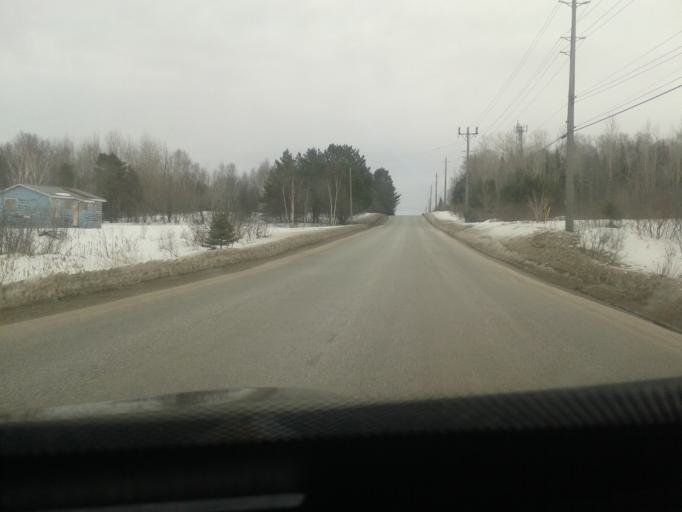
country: CA
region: Ontario
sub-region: Nipissing District
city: North Bay
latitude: 46.3471
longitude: -79.4799
